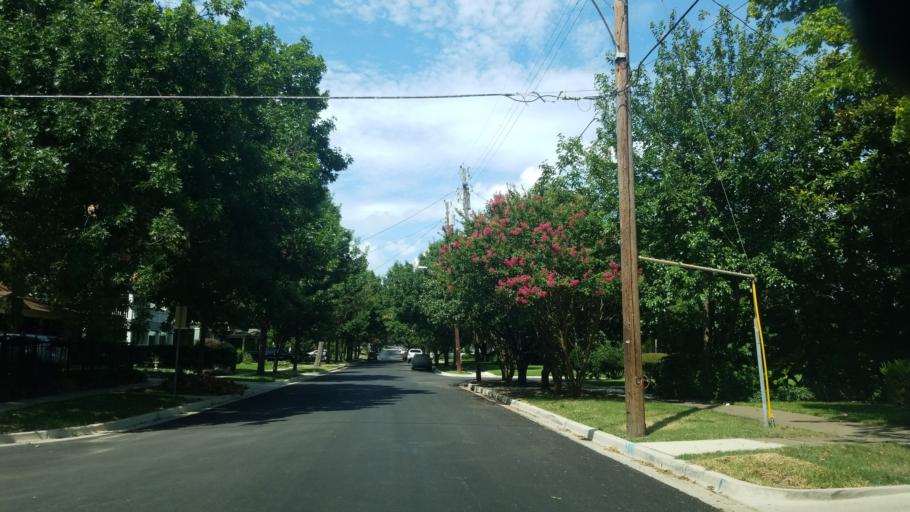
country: US
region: Texas
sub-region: Dallas County
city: Dallas
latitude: 32.7990
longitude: -96.7735
